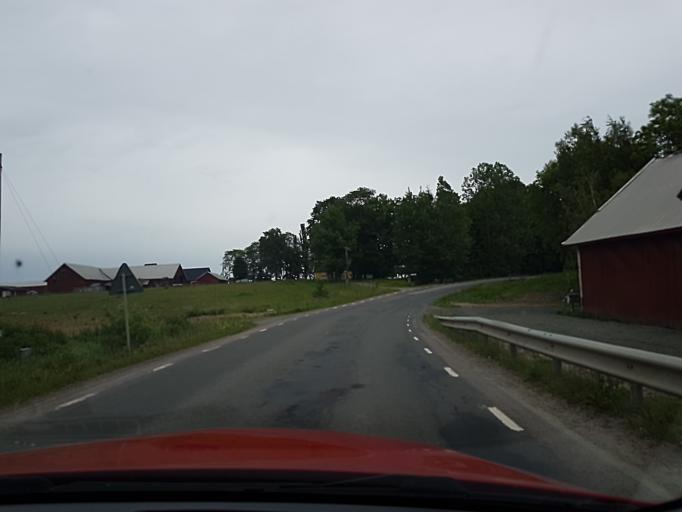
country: SE
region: Vaestra Goetaland
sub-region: Skovde Kommun
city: Skoevde
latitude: 58.3876
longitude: 13.9048
